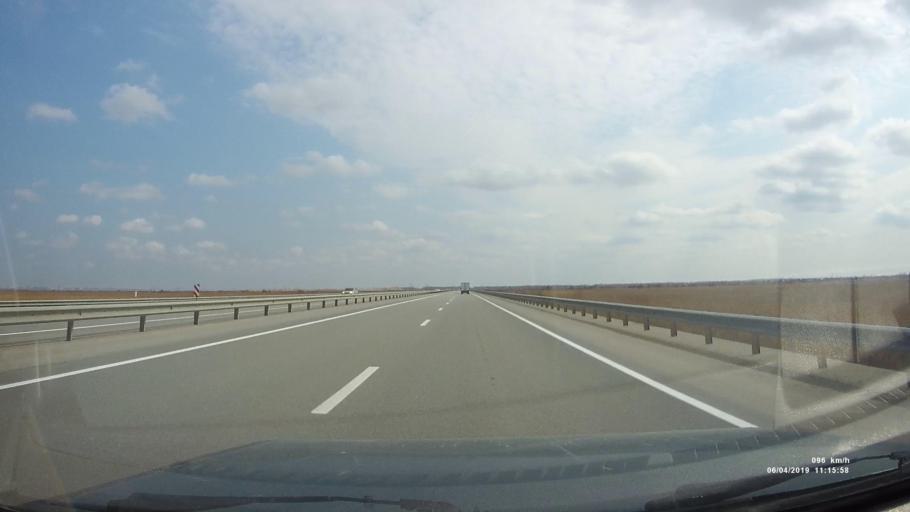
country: RU
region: Rostov
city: Kuleshovka
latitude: 47.0906
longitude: 39.5537
